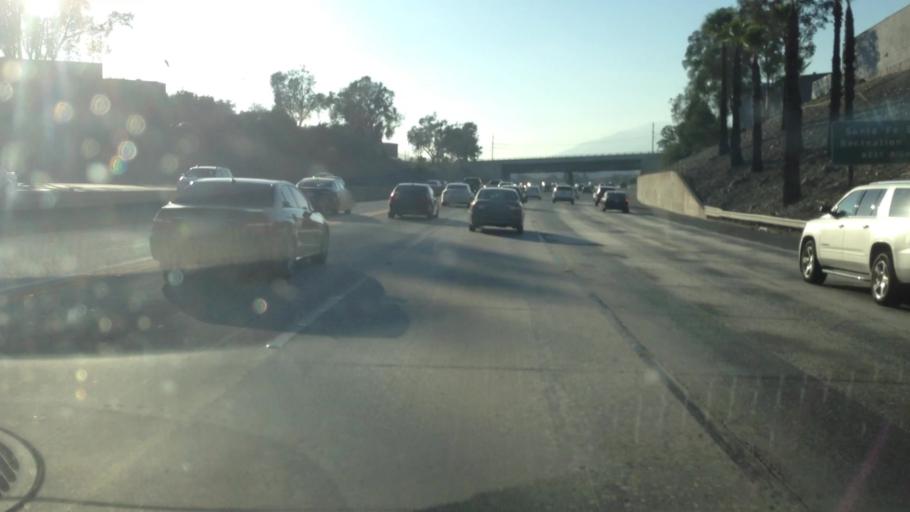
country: US
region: California
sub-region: Los Angeles County
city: Azusa
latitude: 34.1289
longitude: -117.9223
